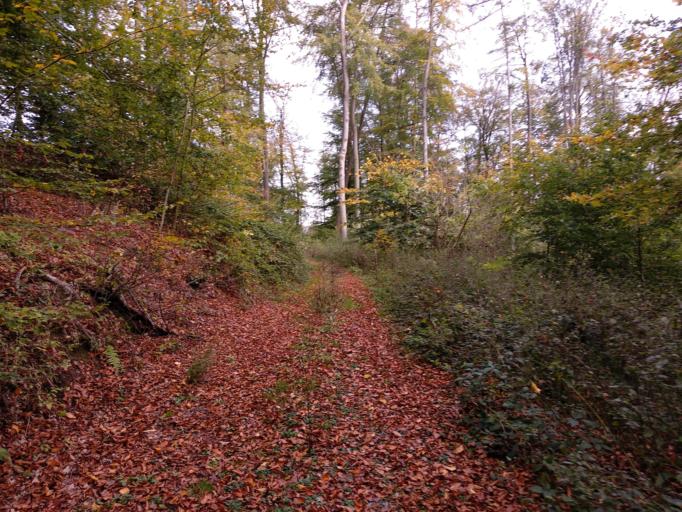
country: DE
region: North Rhine-Westphalia
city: Beverungen
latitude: 51.6863
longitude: 9.3742
